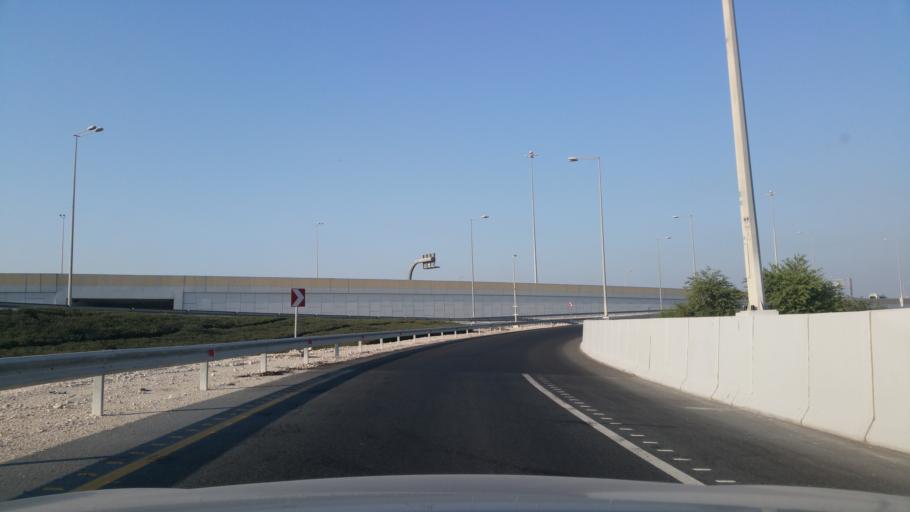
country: QA
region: Al Wakrah
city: Al Wukayr
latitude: 25.1621
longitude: 51.5690
